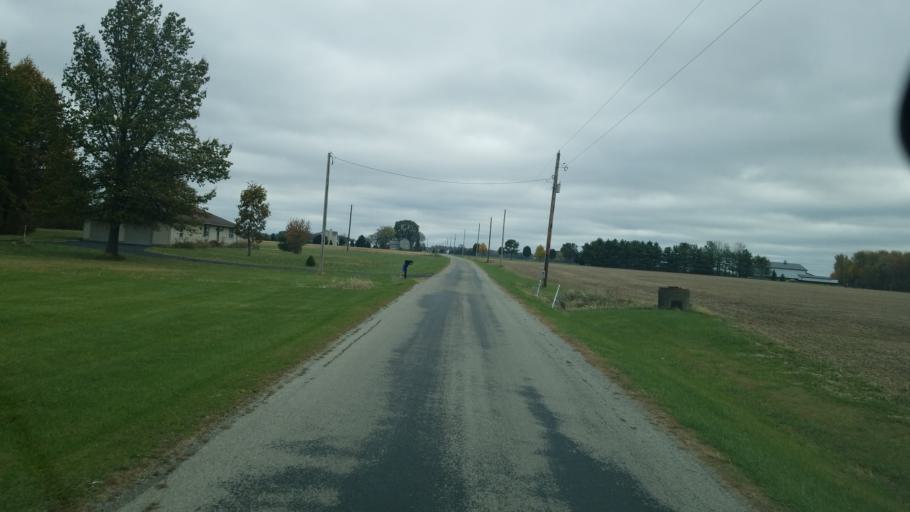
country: US
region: Ohio
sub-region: Huron County
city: Willard
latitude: 40.9315
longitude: -82.8378
